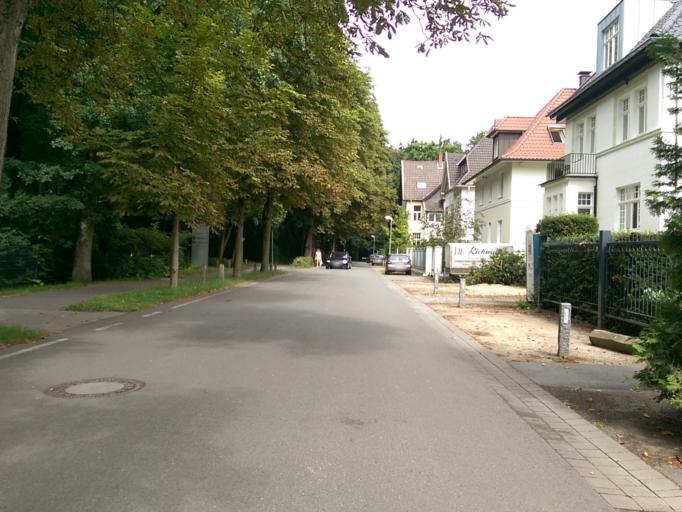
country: DE
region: North Rhine-Westphalia
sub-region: Regierungsbezirk Detmold
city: Guetersloh
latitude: 51.8979
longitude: 8.3873
